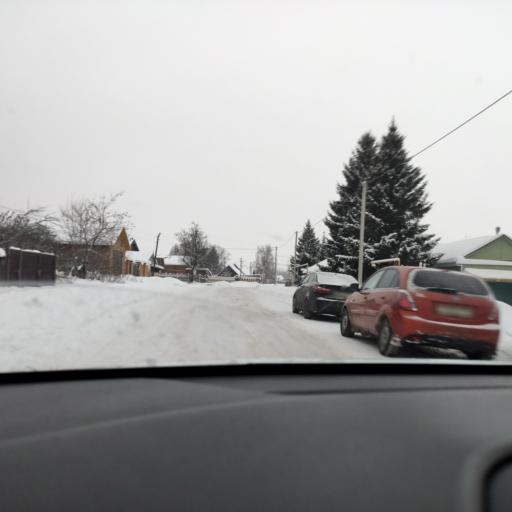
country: RU
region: Tatarstan
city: Vysokaya Gora
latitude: 55.9554
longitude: 49.1597
